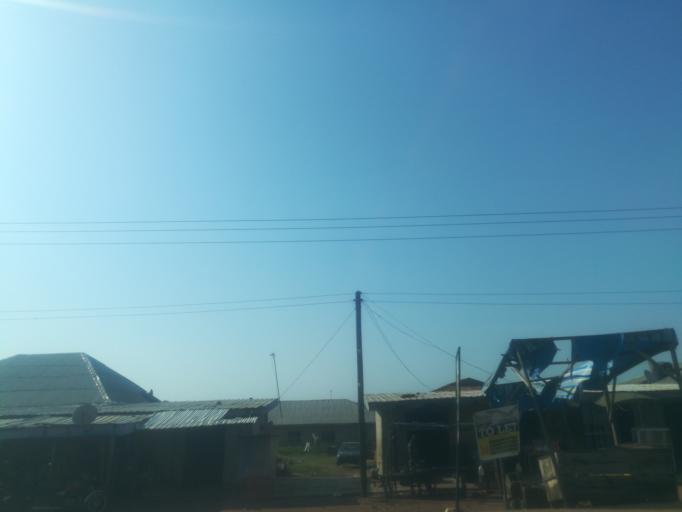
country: NG
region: Ogun
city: Abeokuta
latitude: 7.1749
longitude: 3.2751
